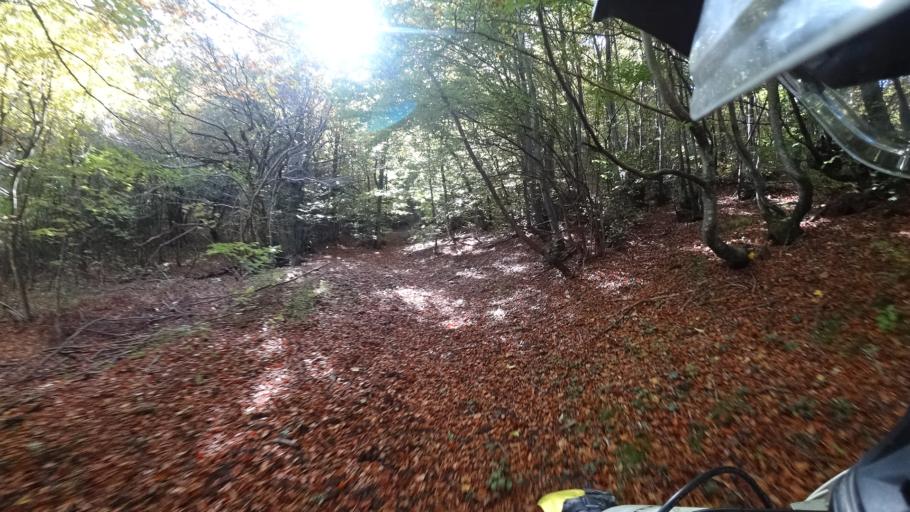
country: HR
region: Karlovacka
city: Plaski
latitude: 45.0801
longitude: 15.3210
